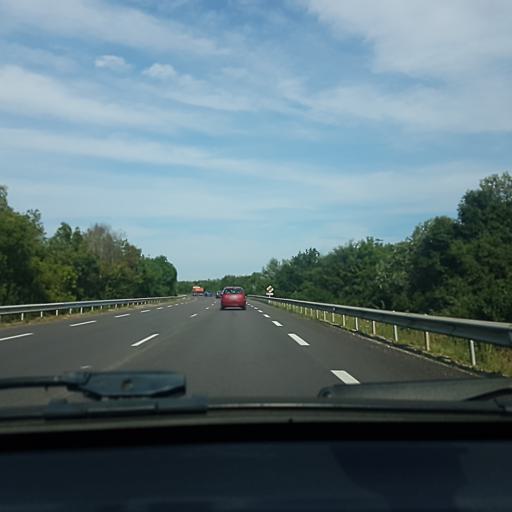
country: FR
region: Bourgogne
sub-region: Departement de Saone-et-Loire
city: Saint-Marcel
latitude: 46.7614
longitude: 4.8878
